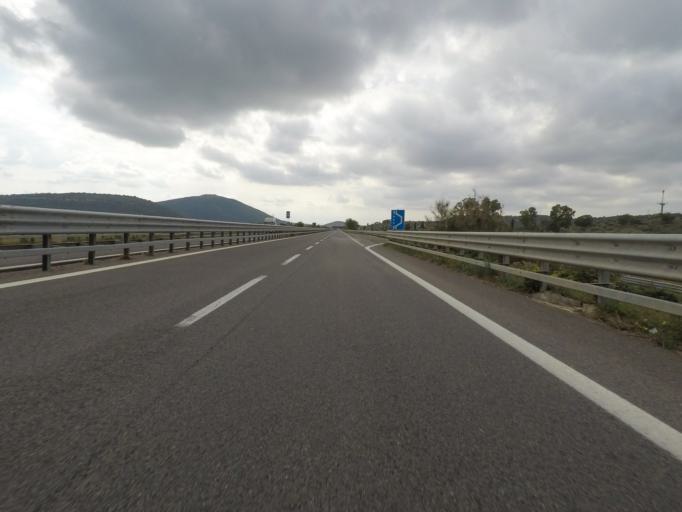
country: IT
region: Tuscany
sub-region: Provincia di Grosseto
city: Bagno Roselle
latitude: 42.8461
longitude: 11.1560
